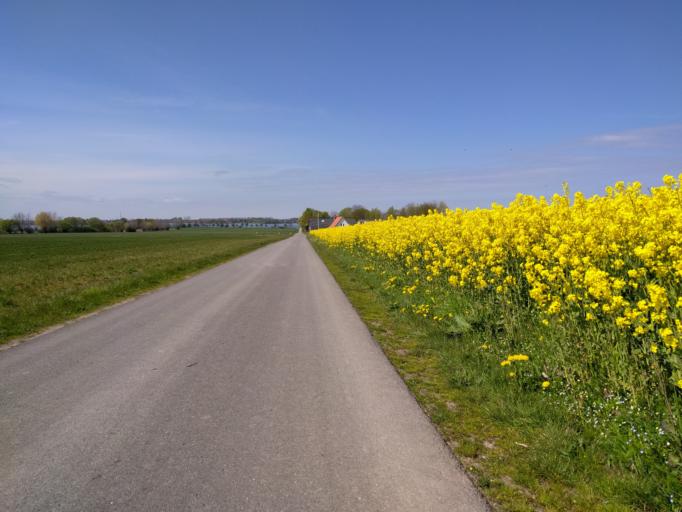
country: DK
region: South Denmark
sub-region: Kerteminde Kommune
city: Munkebo
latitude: 55.4455
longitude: 10.5925
